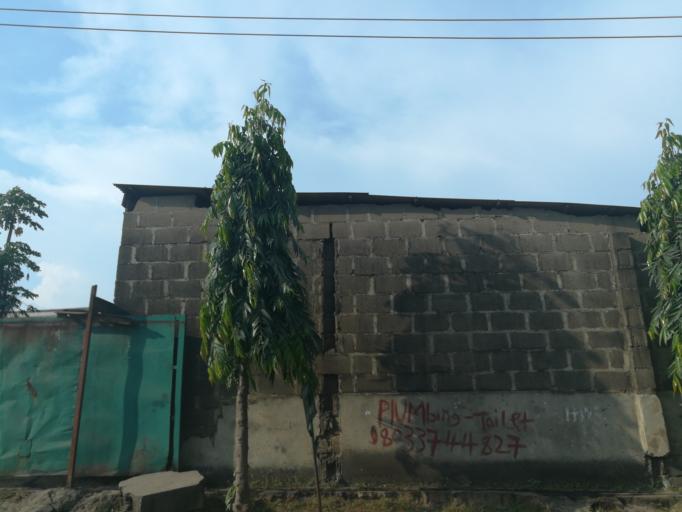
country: NG
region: Lagos
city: Ojota
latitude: 6.5965
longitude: 3.3972
